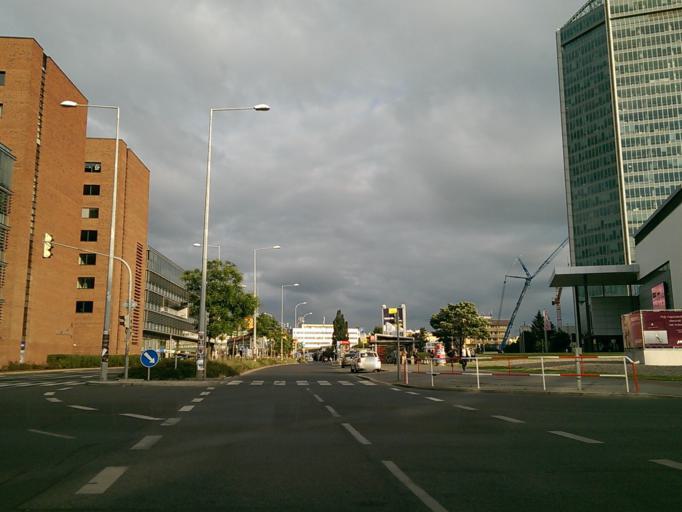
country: CZ
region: Praha
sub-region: Praha 2
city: Vysehrad
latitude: 50.0521
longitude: 14.4391
